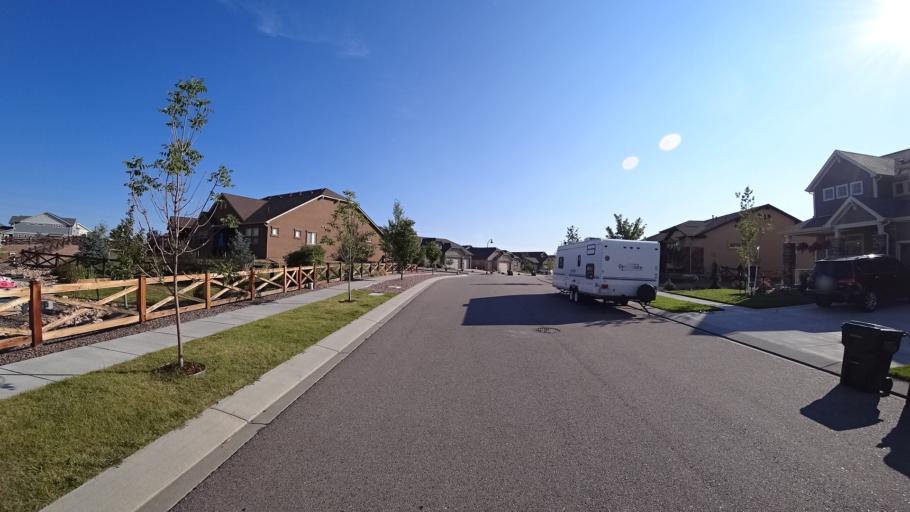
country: US
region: Colorado
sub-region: El Paso County
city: Cimarron Hills
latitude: 38.9356
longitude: -104.6696
